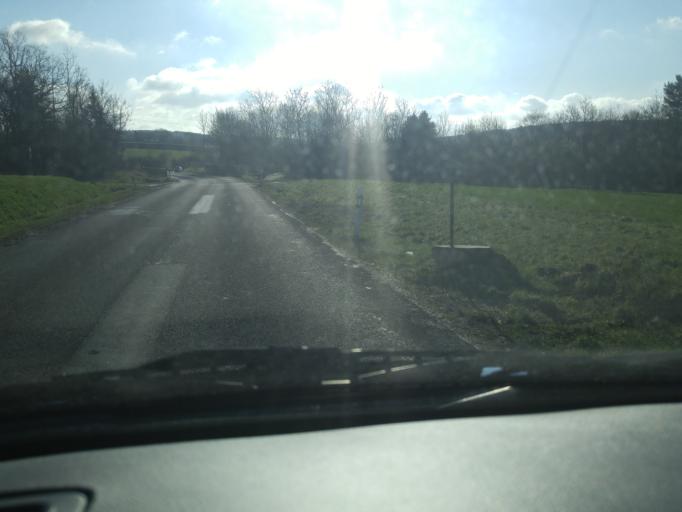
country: DE
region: Hesse
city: Herbstein
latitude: 50.5821
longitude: 9.3599
